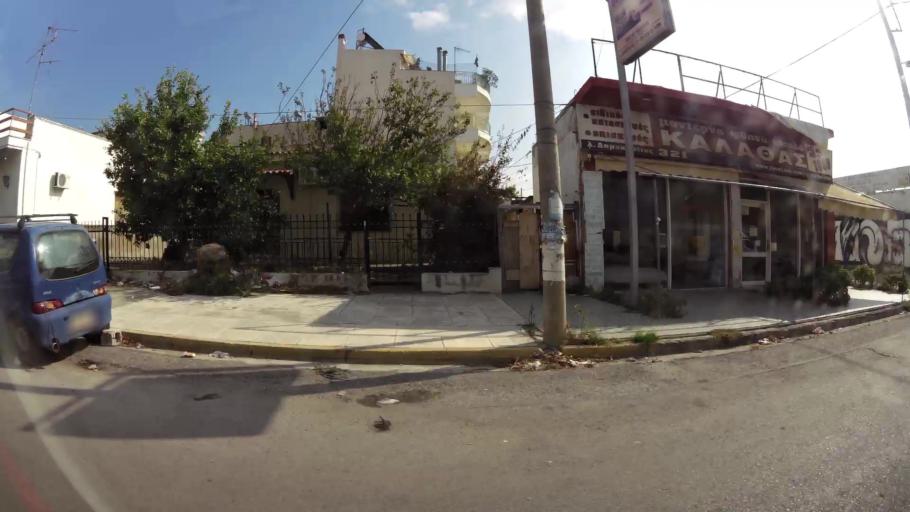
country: GR
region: Attica
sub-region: Nomarchia Dytikis Attikis
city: Zefyri
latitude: 38.0542
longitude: 23.7305
